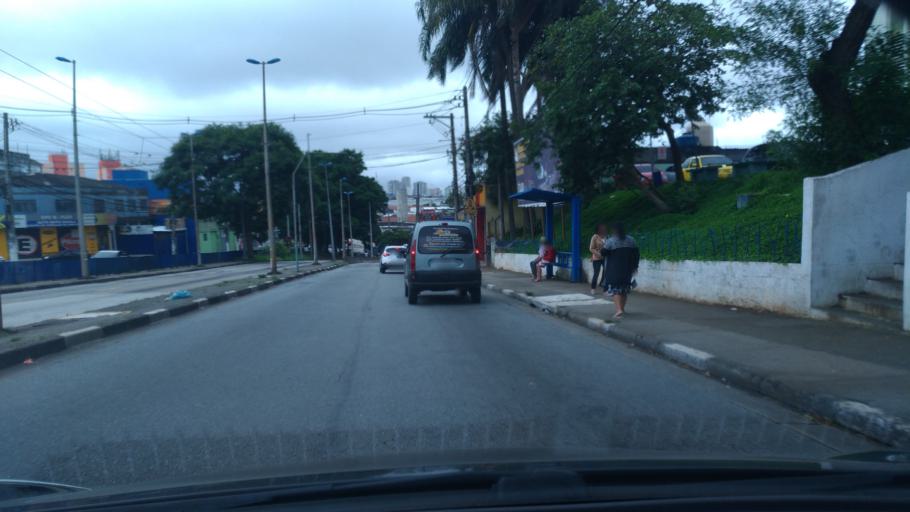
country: BR
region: Sao Paulo
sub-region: Sao Bernardo Do Campo
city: Sao Bernardo do Campo
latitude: -23.6916
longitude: -46.5871
